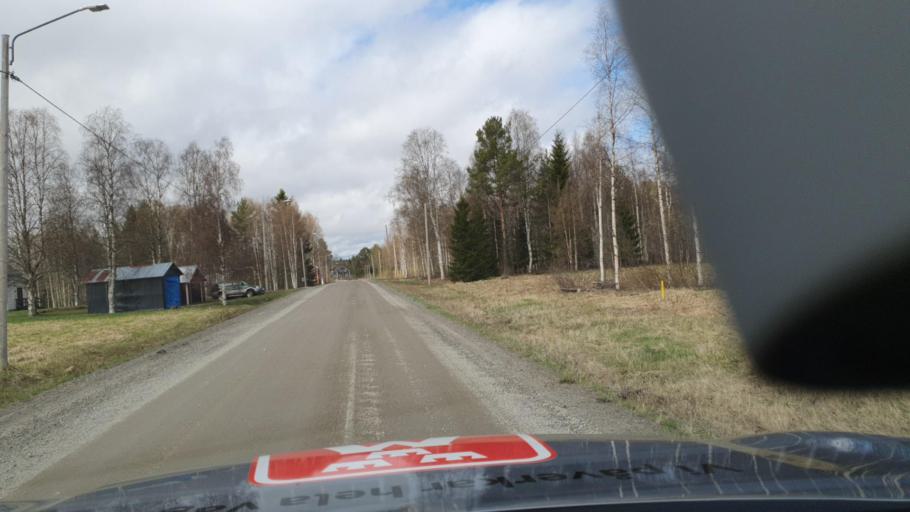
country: SE
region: Vaesterbotten
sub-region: Bjurholms Kommun
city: Bjurholm
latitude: 63.6955
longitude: 18.9544
